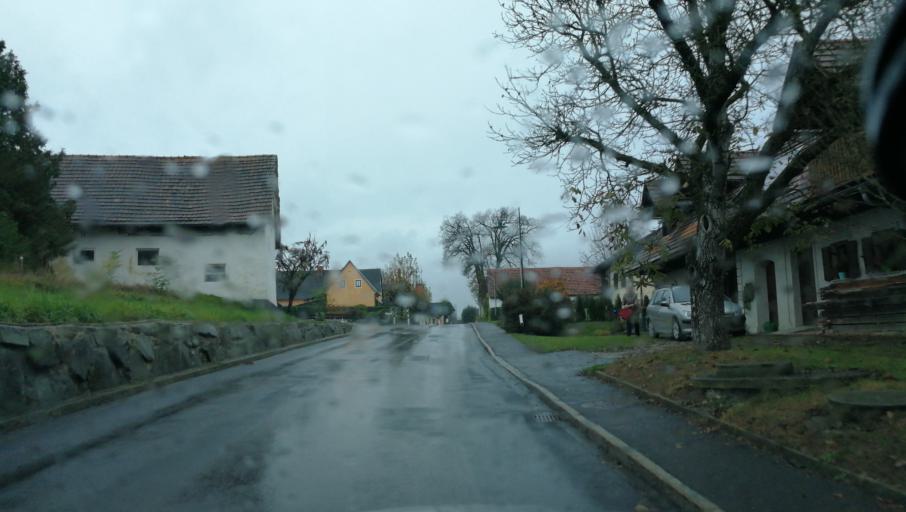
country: AT
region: Styria
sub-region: Politischer Bezirk Suedoststeiermark
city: Weinburg am Sassbach
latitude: 46.7342
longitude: 15.7121
